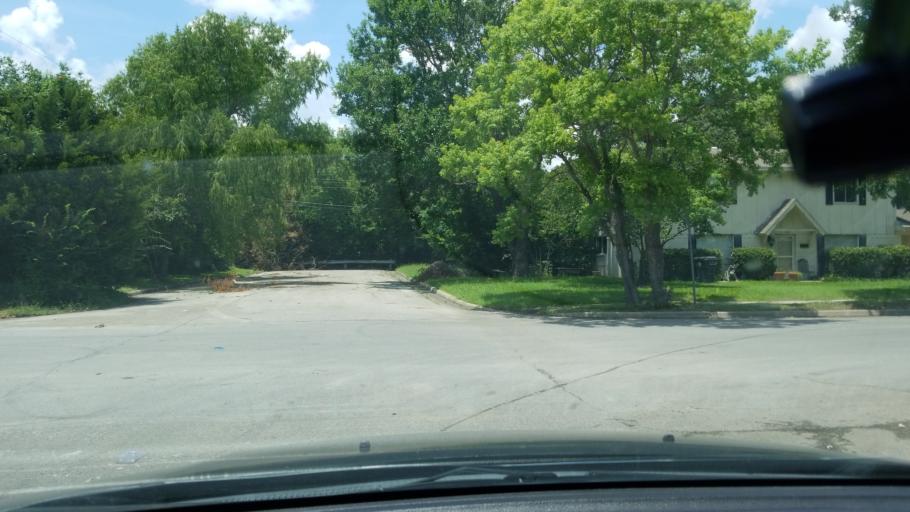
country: US
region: Texas
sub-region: Dallas County
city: Balch Springs
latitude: 32.7400
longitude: -96.6520
